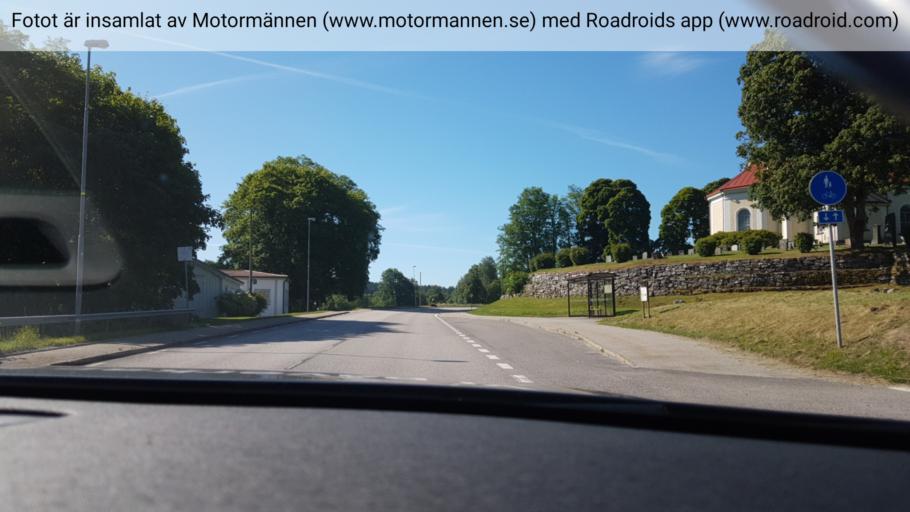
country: SE
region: Vaestra Goetaland
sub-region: Ulricehamns Kommun
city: Ulricehamn
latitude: 57.9280
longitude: 13.4934
